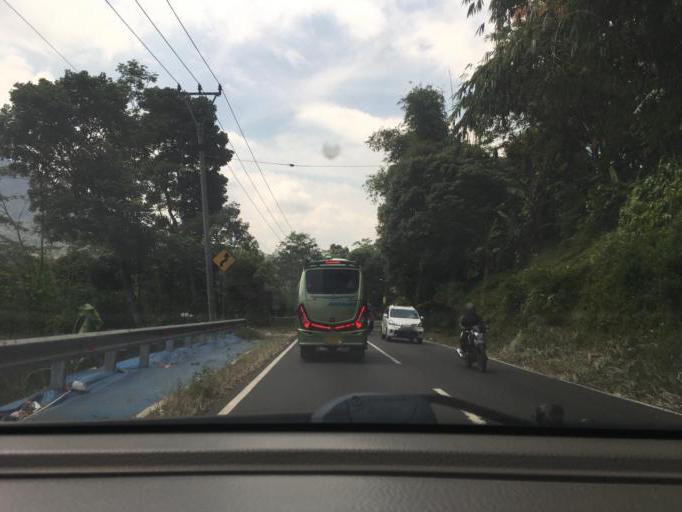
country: ID
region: West Java
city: Wage Cibahayu
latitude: -7.1163
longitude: 108.1204
